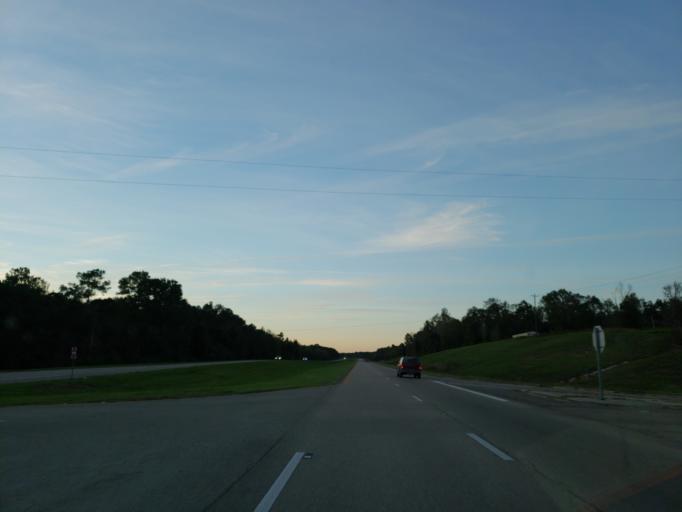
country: US
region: Mississippi
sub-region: Wayne County
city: Belmont
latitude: 31.5899
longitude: -88.5487
